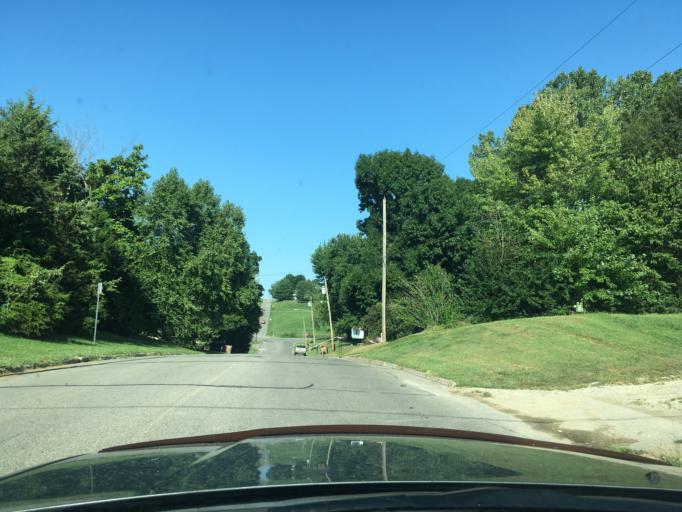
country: US
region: Kansas
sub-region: Atchison County
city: Atchison
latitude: 39.5802
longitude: -95.1316
